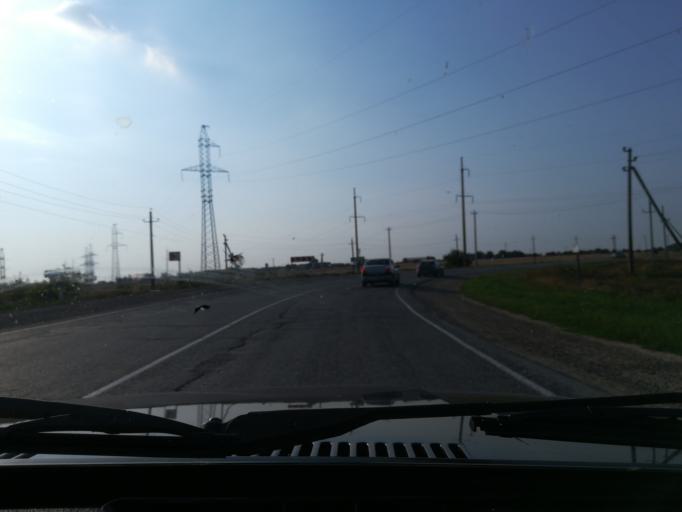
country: RU
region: Krasnodarskiy
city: Yurovka
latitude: 45.1043
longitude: 37.4224
